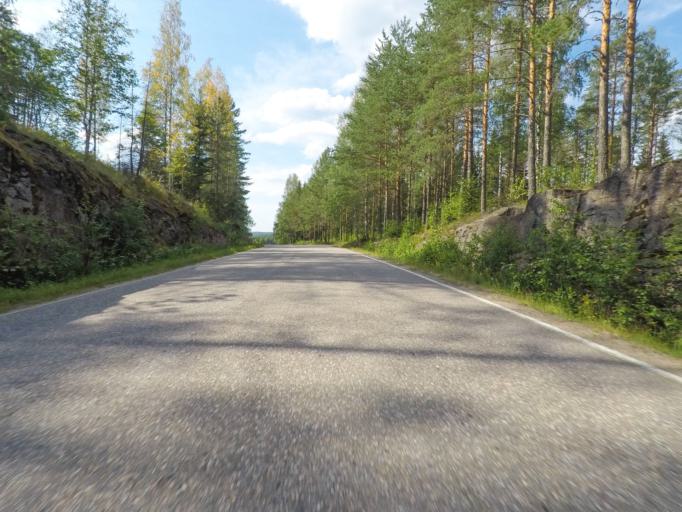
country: FI
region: Southern Savonia
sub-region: Mikkeli
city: Puumala
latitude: 61.6849
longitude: 28.2286
